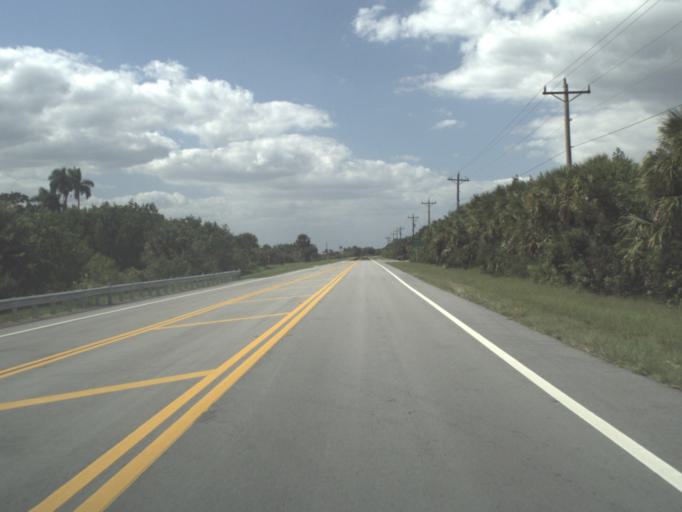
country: US
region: Florida
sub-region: Collier County
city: Marco
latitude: 25.9407
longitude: -81.4675
